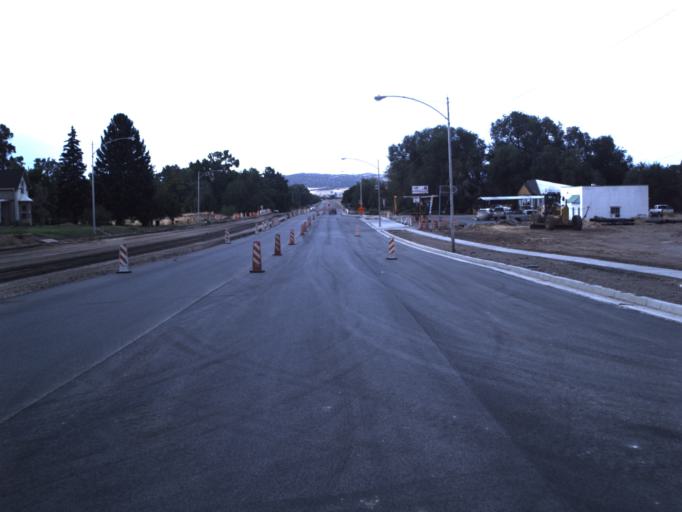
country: US
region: Utah
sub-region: Millard County
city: Fillmore
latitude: 38.9733
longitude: -112.3236
